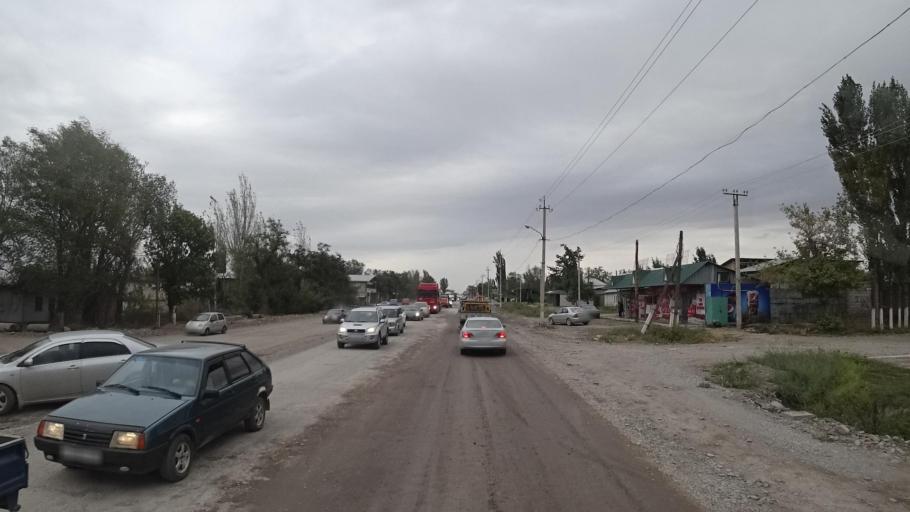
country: KG
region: Chuy
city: Sokuluk
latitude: 42.8535
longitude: 74.2118
